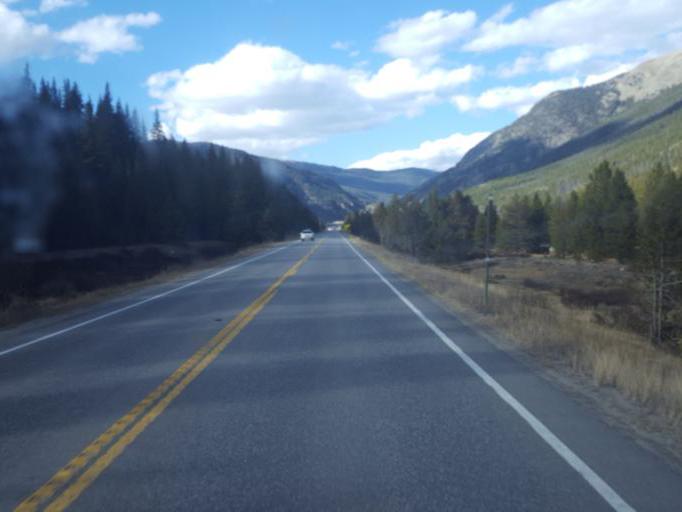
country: US
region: Colorado
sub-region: Summit County
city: Frisco
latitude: 39.4869
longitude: -106.1345
